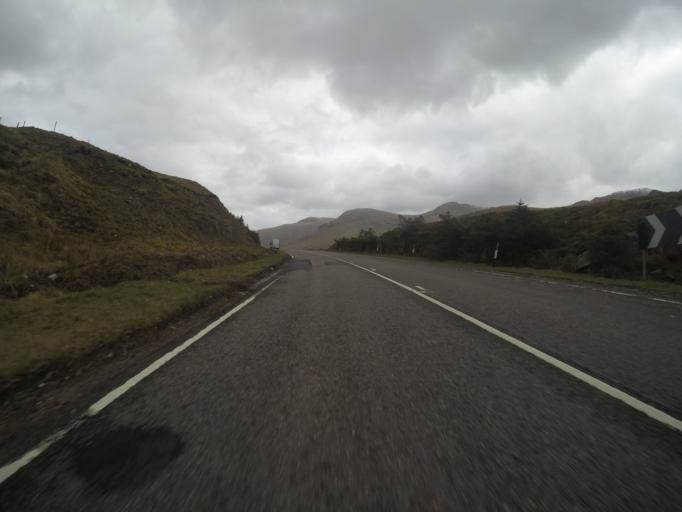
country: GB
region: Scotland
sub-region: Highland
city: Fort William
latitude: 57.1545
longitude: -5.2444
